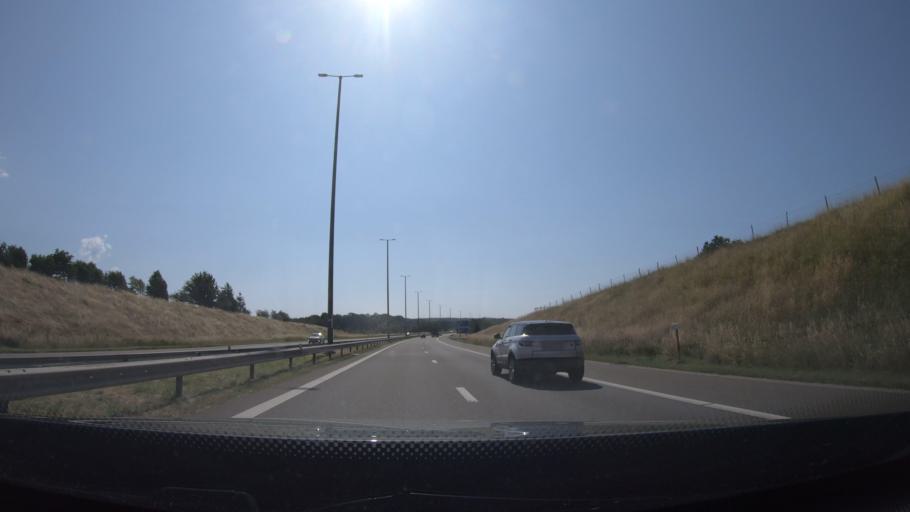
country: BE
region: Wallonia
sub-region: Province de Liege
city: Jalhay
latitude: 50.5234
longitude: 5.9349
